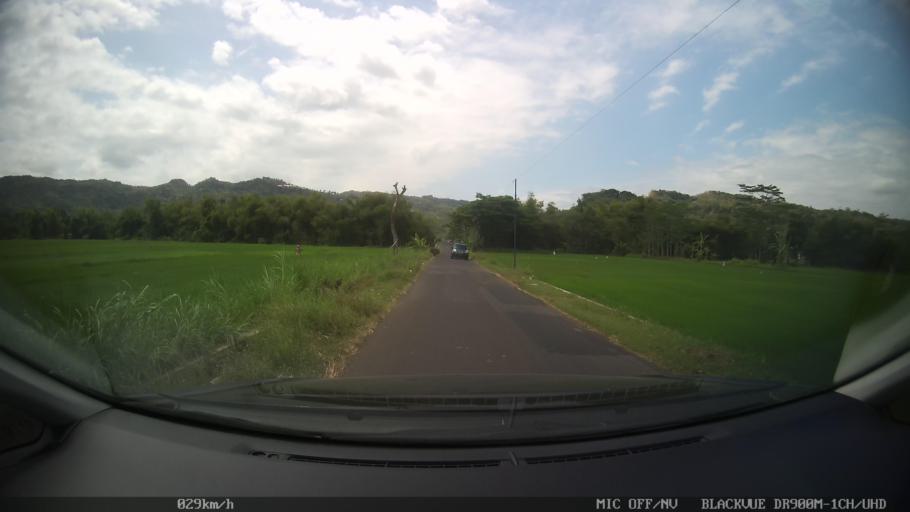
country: ID
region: Central Java
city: Candi Prambanan
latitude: -7.8111
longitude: 110.5023
